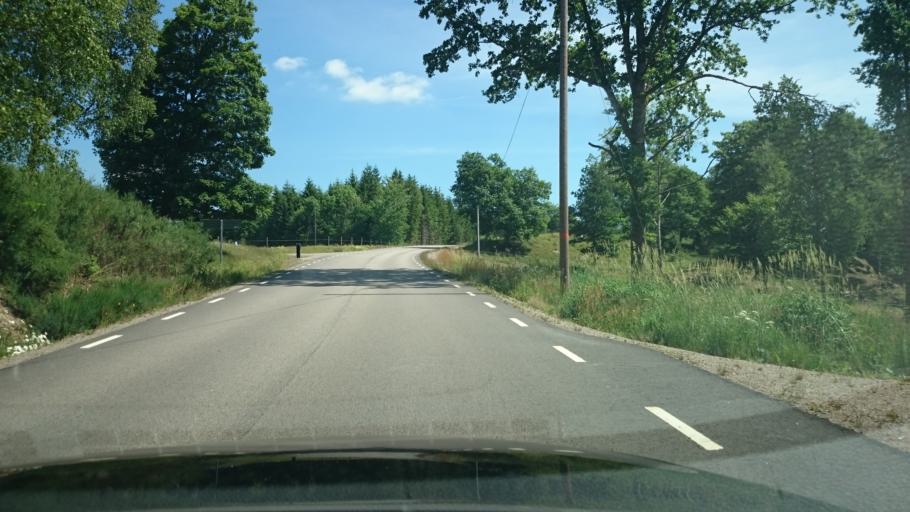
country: SE
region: Halland
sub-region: Hylte Kommun
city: Torup
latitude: 56.9577
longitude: 13.1609
